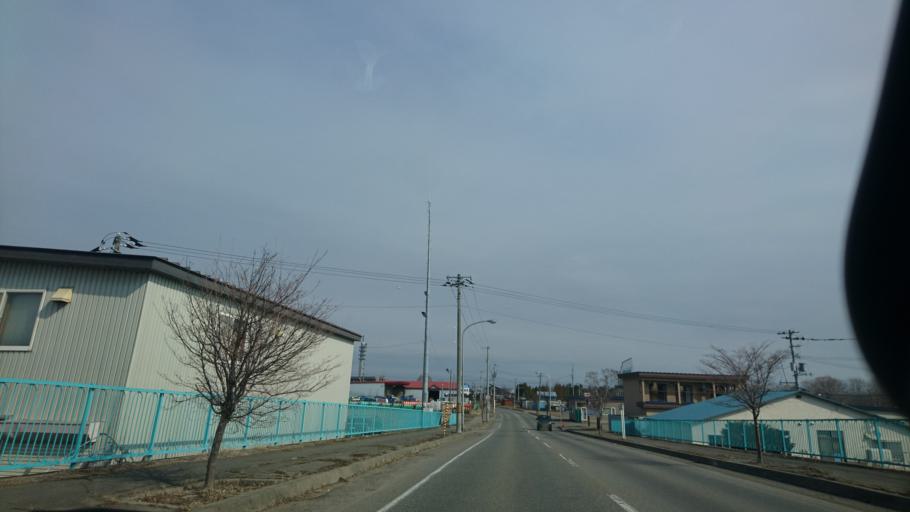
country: JP
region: Hokkaido
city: Obihiro
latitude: 42.9502
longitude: 143.2077
